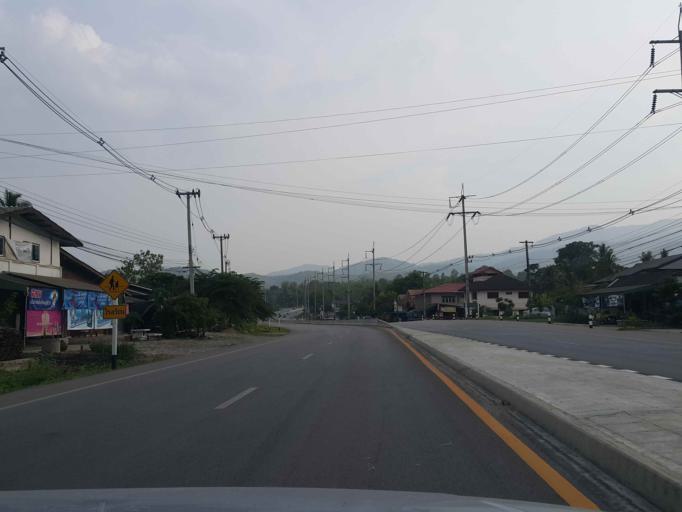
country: TH
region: Chiang Mai
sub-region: Amphoe Chiang Dao
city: Chiang Dao
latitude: 19.3279
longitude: 98.9545
